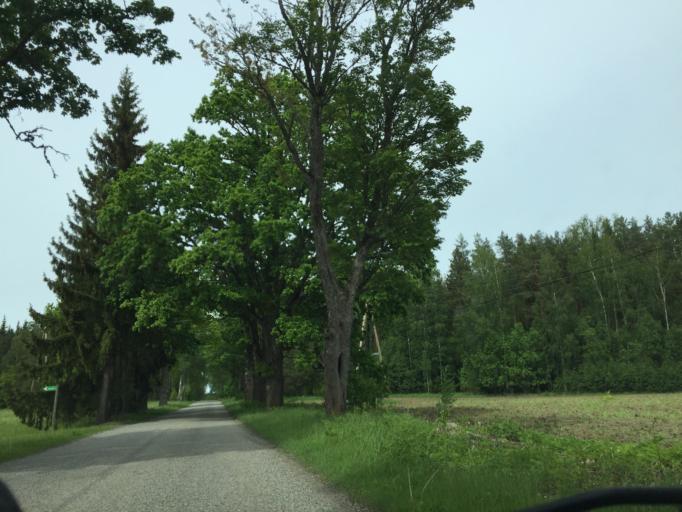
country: LV
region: Koceni
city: Koceni
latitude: 57.4874
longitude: 25.3645
